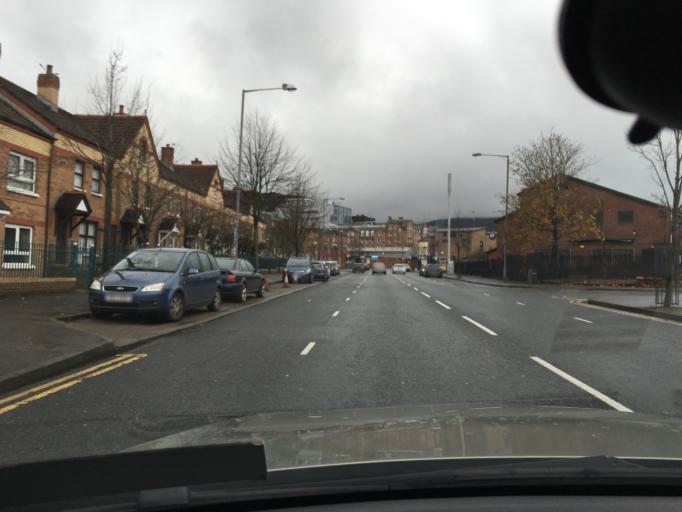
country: GB
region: Northern Ireland
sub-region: City of Belfast
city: Belfast
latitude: 54.5952
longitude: -5.9487
